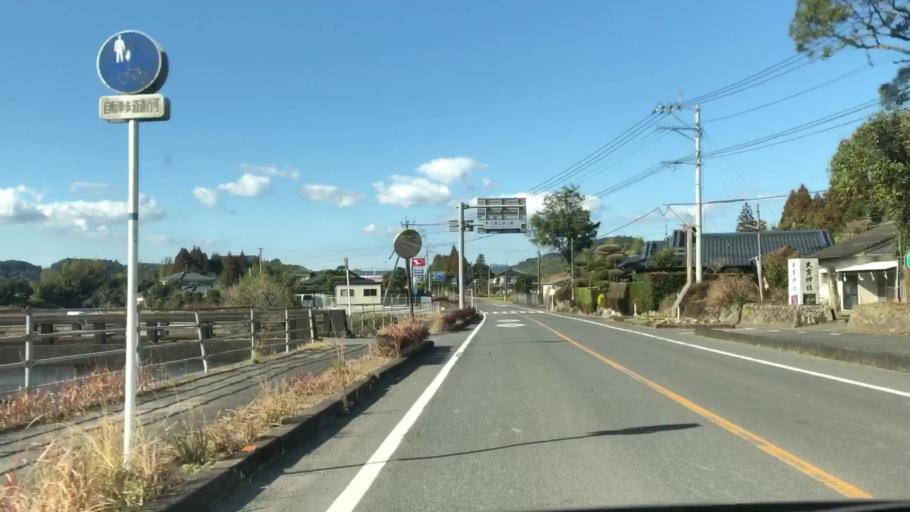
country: JP
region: Kagoshima
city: Satsumasendai
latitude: 31.7967
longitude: 130.4412
